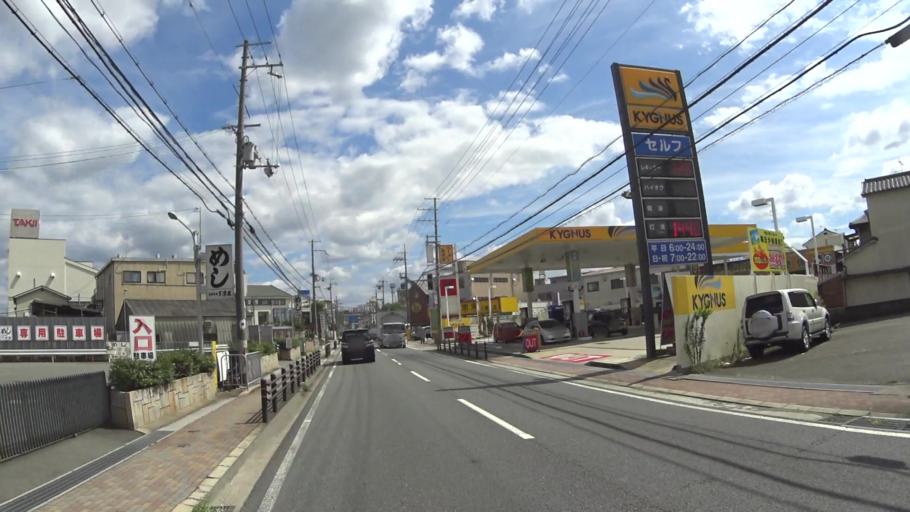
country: JP
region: Kyoto
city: Yawata
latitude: 34.8777
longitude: 135.7411
